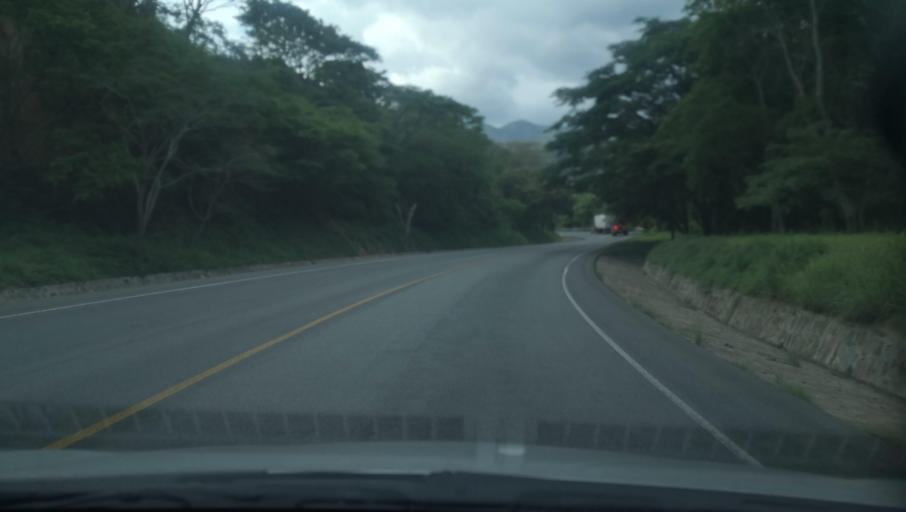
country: NI
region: Nueva Segovia
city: Ocotal
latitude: 13.6792
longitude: -86.4885
